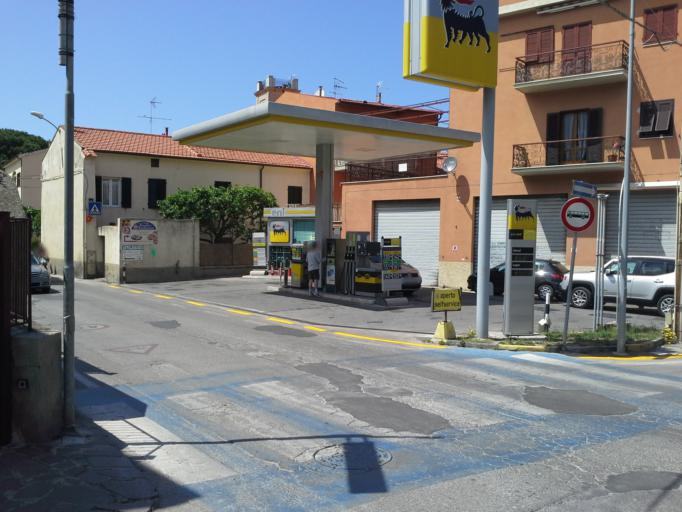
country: IT
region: Tuscany
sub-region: Provincia di Livorno
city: Marciana Marina
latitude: 42.8043
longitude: 10.1996
